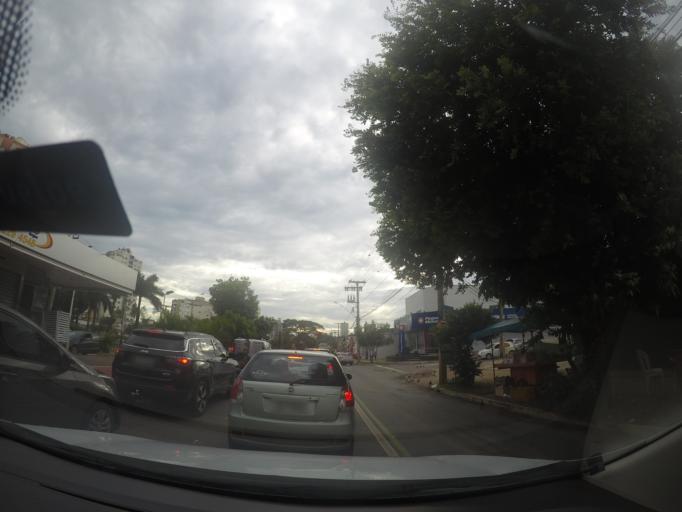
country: BR
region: Goias
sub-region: Goiania
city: Goiania
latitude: -16.6798
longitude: -49.2533
